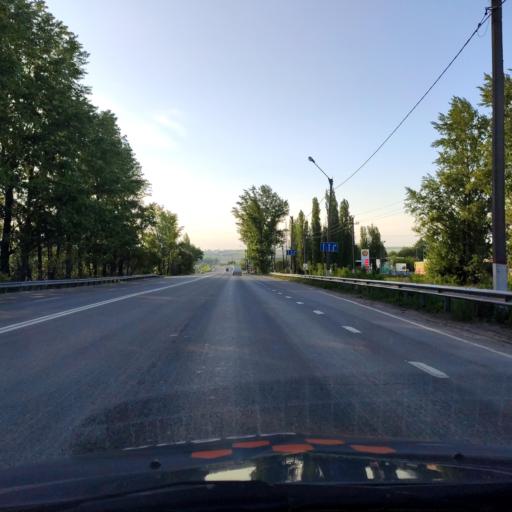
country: RU
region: Lipetsk
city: Yelets
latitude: 52.5937
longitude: 38.4858
